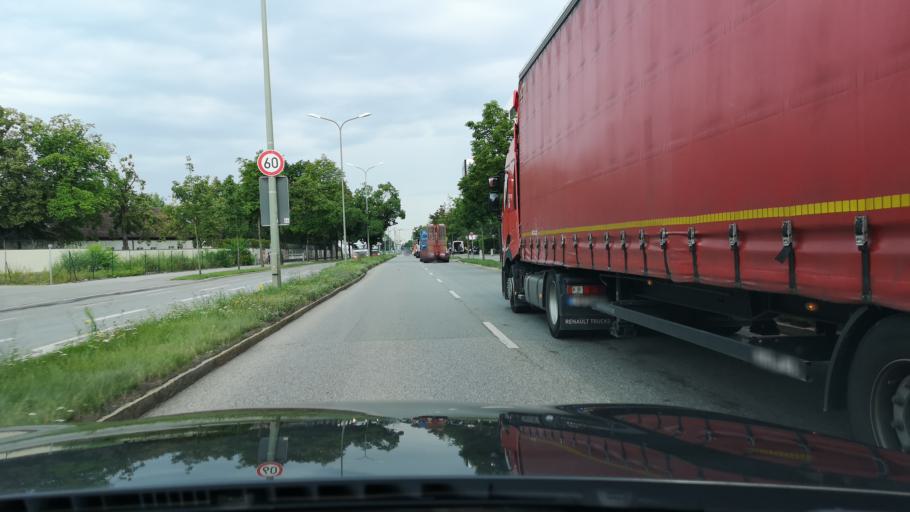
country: DE
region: Bavaria
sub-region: Upper Bavaria
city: Bogenhausen
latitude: 48.1870
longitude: 11.6020
